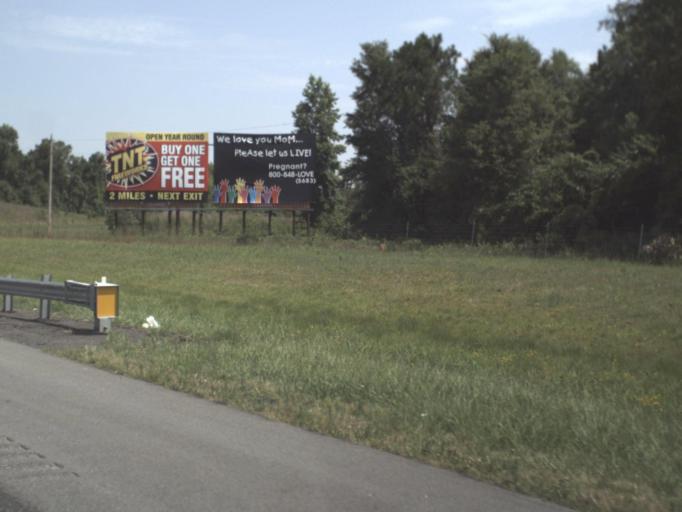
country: US
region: Georgia
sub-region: Echols County
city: Statenville
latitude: 30.5720
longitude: -83.0974
